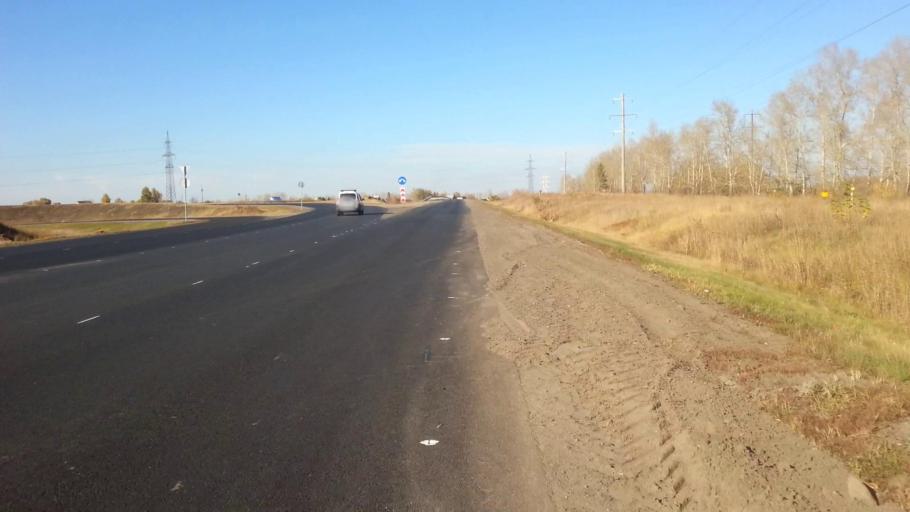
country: RU
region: Altai Krai
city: Sannikovo
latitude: 53.3382
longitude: 83.9387
